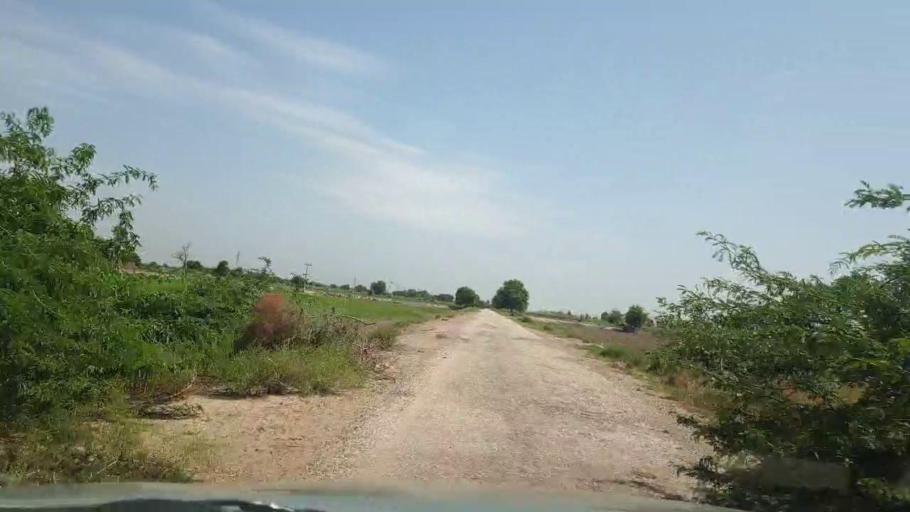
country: PK
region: Sindh
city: Bozdar
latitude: 27.0927
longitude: 68.9698
